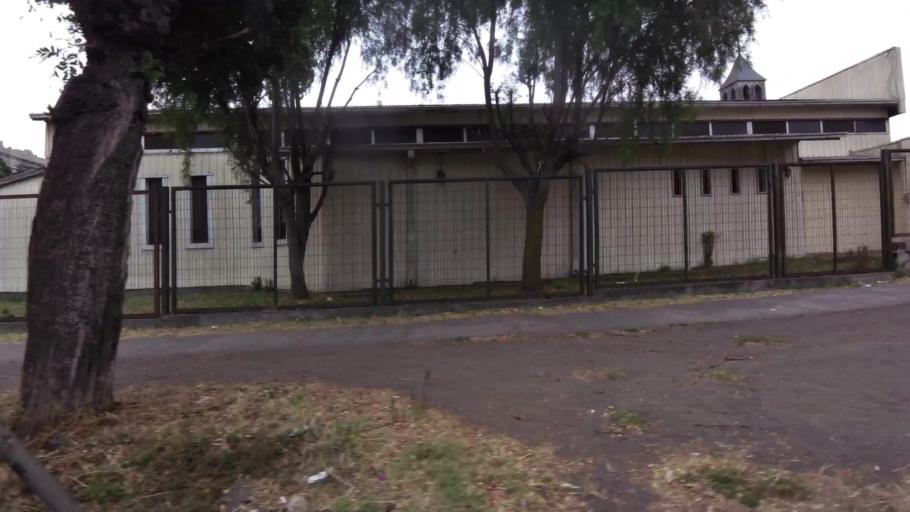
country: CL
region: Biobio
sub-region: Provincia de Concepcion
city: Concepcion
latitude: -36.8152
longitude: -73.0523
